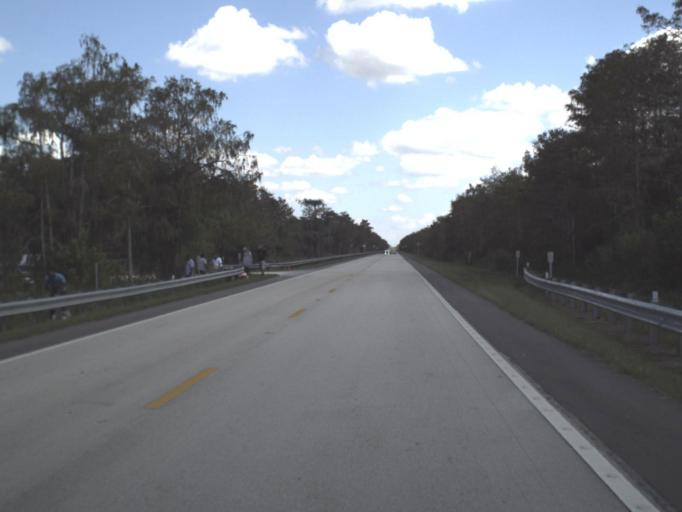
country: US
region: Florida
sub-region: Miami-Dade County
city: Kendall West
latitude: 25.8486
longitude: -80.9515
